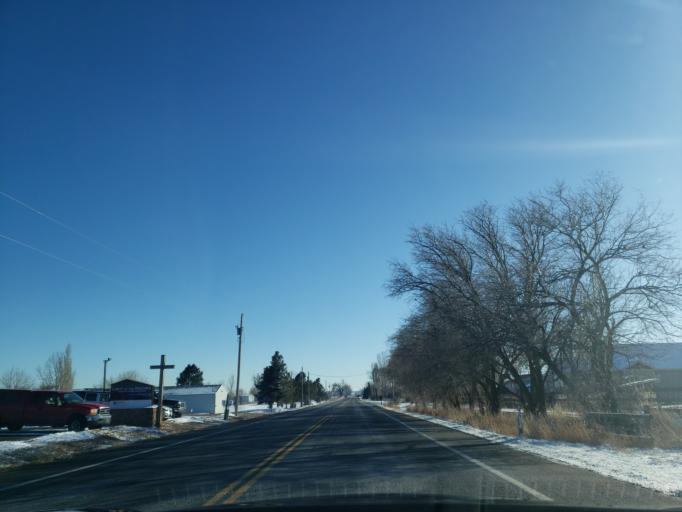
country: US
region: Colorado
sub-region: Weld County
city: Windsor
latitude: 40.5132
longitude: -105.0009
